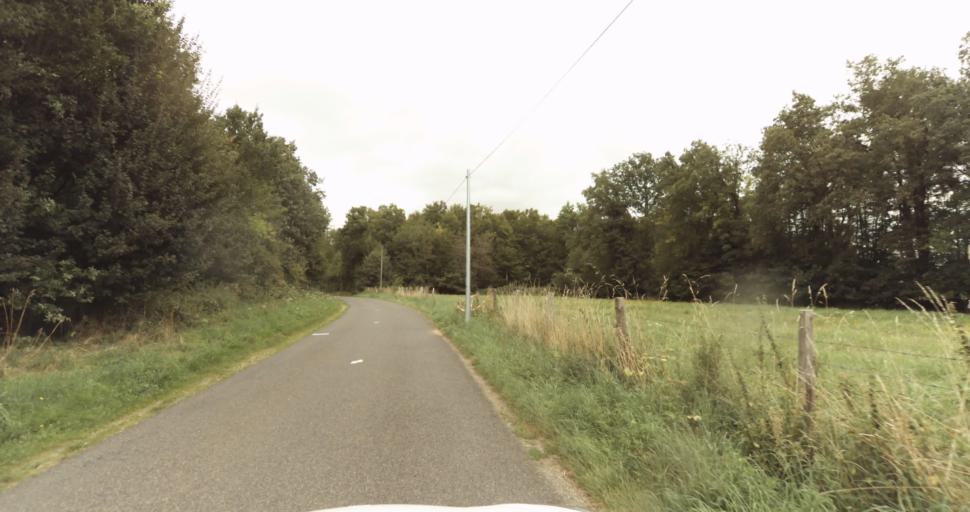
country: FR
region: Haute-Normandie
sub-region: Departement de l'Eure
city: La Madeleine-de-Nonancourt
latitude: 48.8257
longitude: 1.2305
